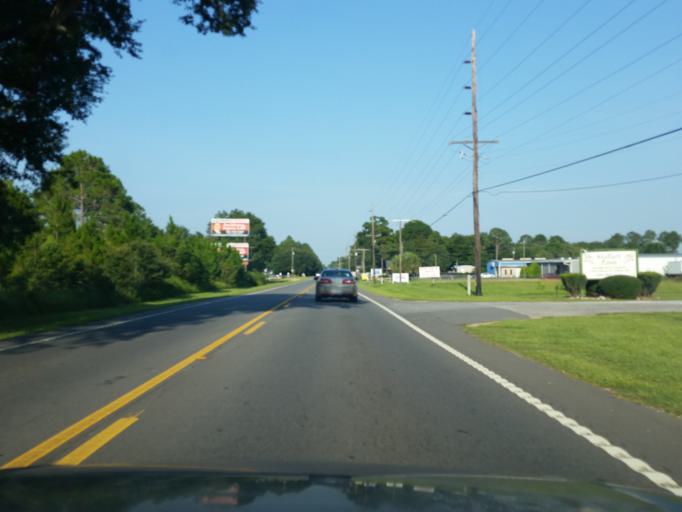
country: US
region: Alabama
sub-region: Baldwin County
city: Foley
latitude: 30.4068
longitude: -87.6447
